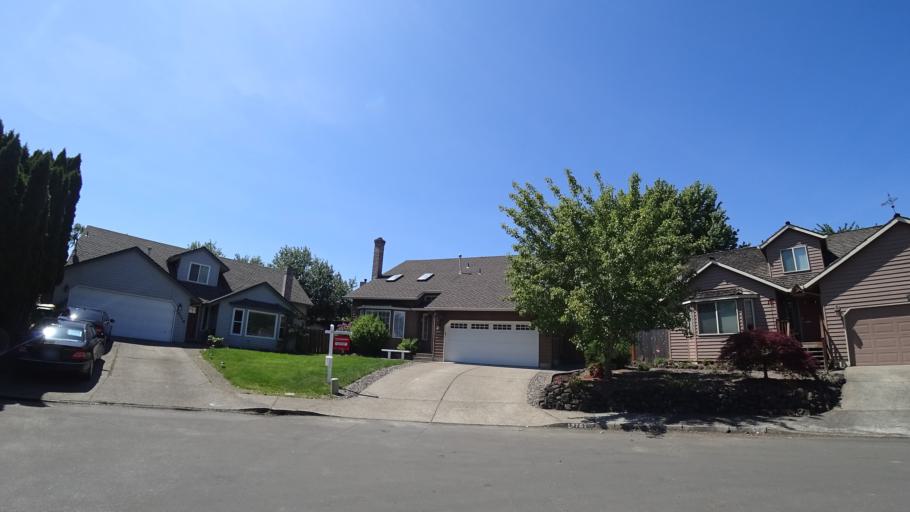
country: US
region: Oregon
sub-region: Washington County
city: Tigard
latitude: 45.4412
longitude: -122.8076
